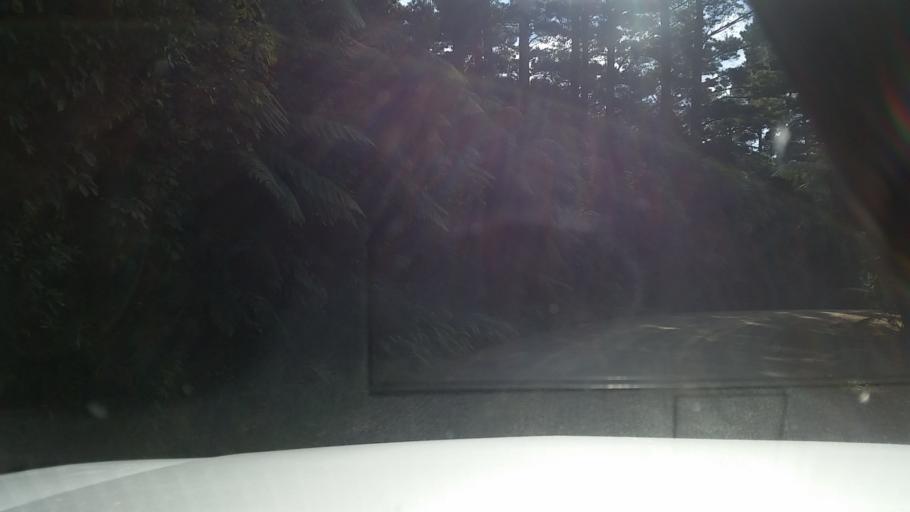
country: NZ
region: Marlborough
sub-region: Marlborough District
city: Picton
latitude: -41.2880
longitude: 174.1748
